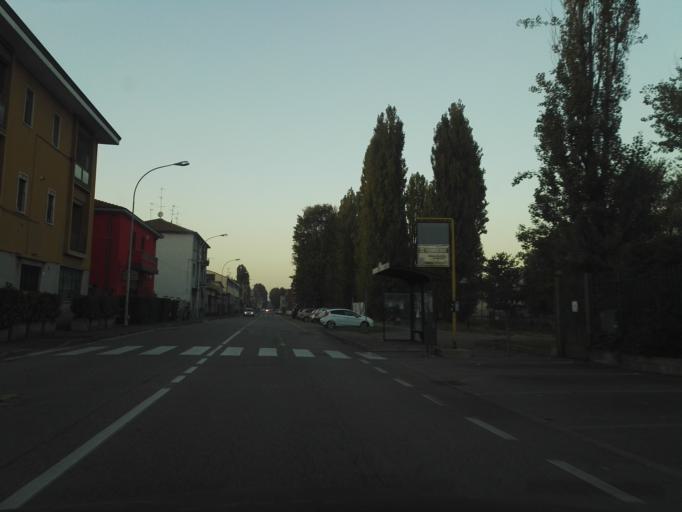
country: IT
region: Lombardy
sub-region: Citta metropolitana di Milano
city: Mezzate
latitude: 45.4383
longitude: 9.2953
